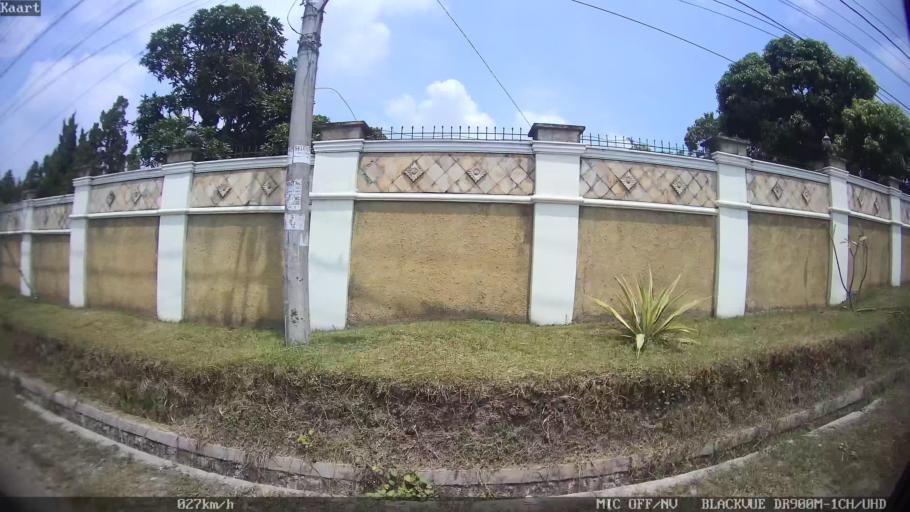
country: ID
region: Lampung
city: Pringsewu
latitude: -5.3405
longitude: 104.9751
